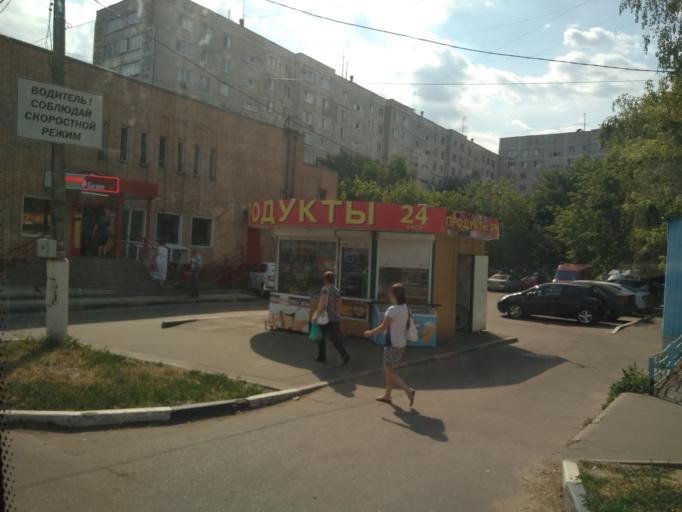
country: RU
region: Moskovskaya
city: Bykovo
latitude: 55.6065
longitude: 38.0749
